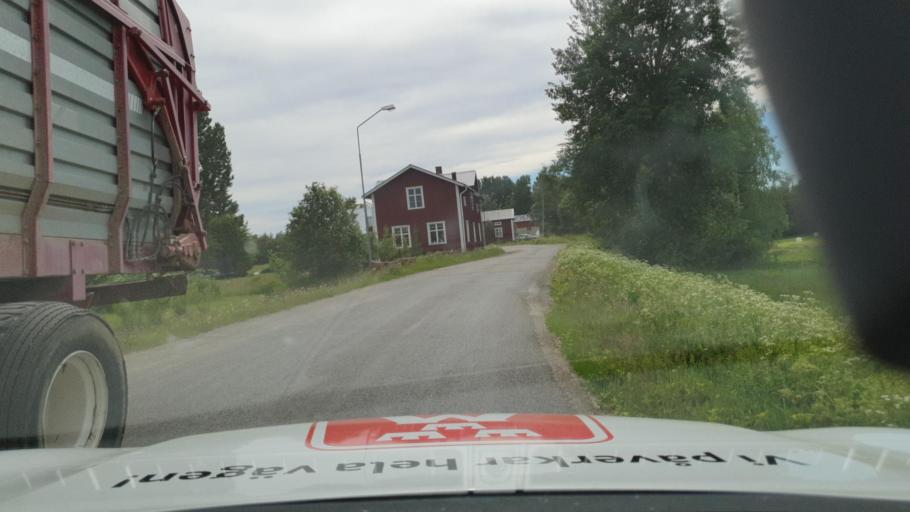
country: SE
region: Vaesterbotten
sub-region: Robertsfors Kommun
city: Robertsfors
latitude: 64.3986
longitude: 21.0214
